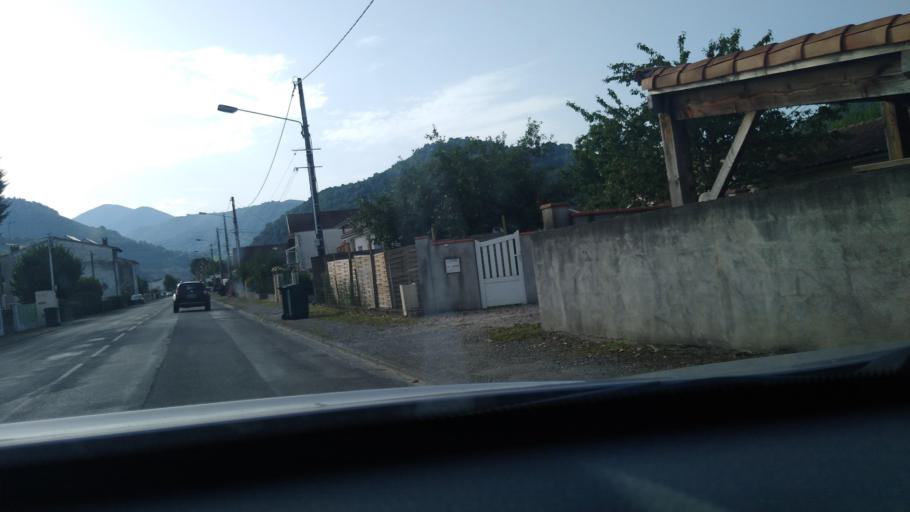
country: FR
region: Midi-Pyrenees
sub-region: Departement de l'Ariege
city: Saint-Girons
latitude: 42.9722
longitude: 1.1560
